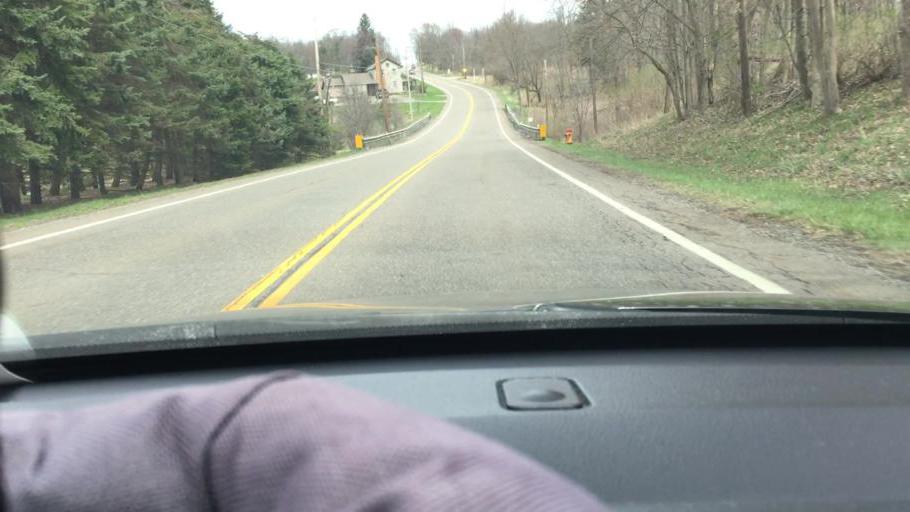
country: US
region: Ohio
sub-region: Columbiana County
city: Columbiana
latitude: 40.9347
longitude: -80.6715
